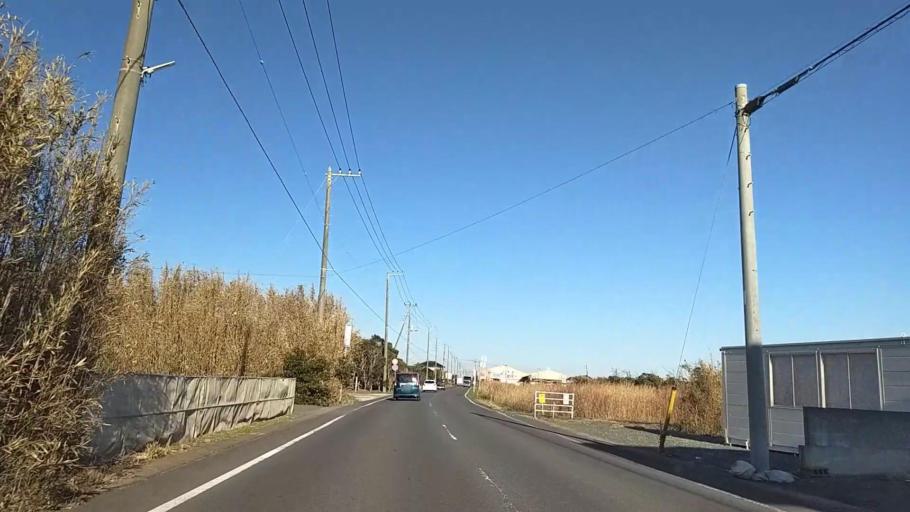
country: JP
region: Chiba
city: Yokaichiba
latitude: 35.6625
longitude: 140.6022
